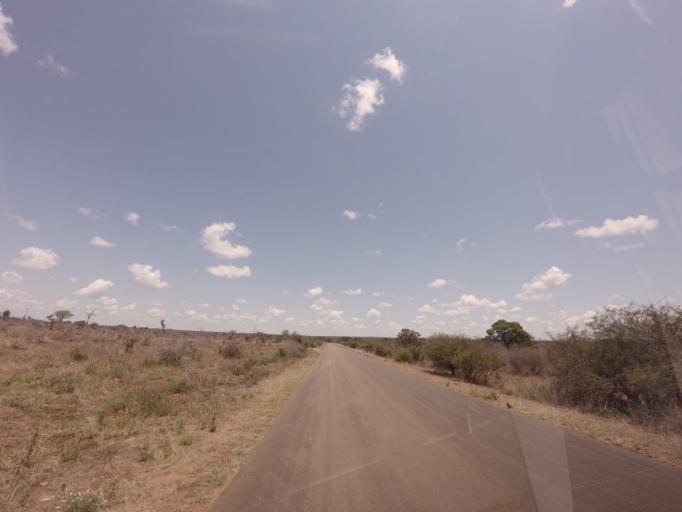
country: ZA
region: Mpumalanga
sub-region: Ehlanzeni District
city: Komatipoort
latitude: -24.8002
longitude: 31.8732
